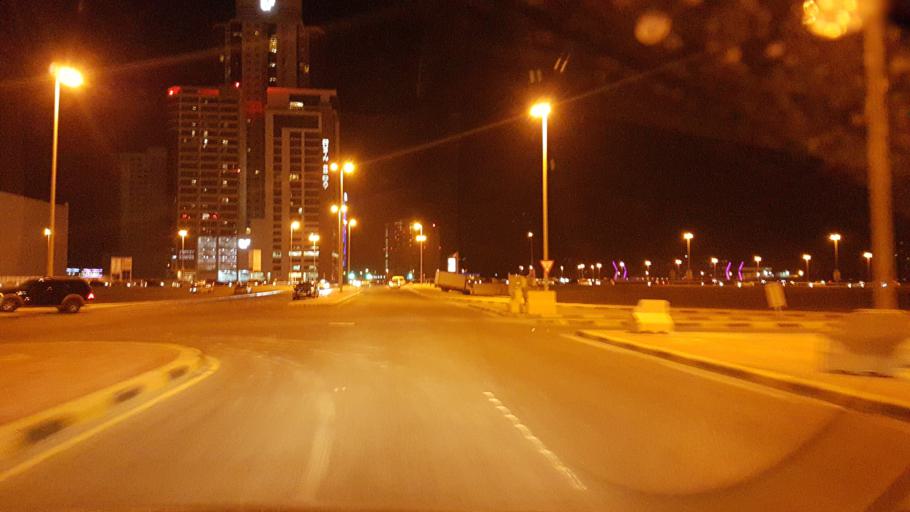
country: BH
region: Manama
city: Jidd Hafs
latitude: 26.2332
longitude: 50.5573
